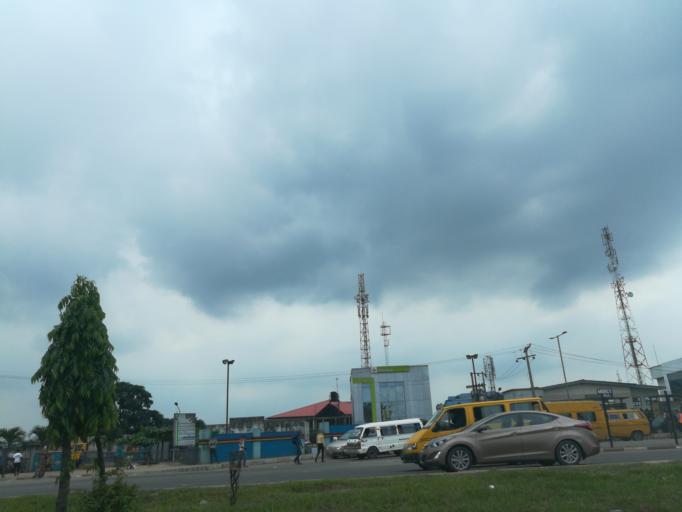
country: NG
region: Lagos
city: Ojota
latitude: 6.5999
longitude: 3.3780
